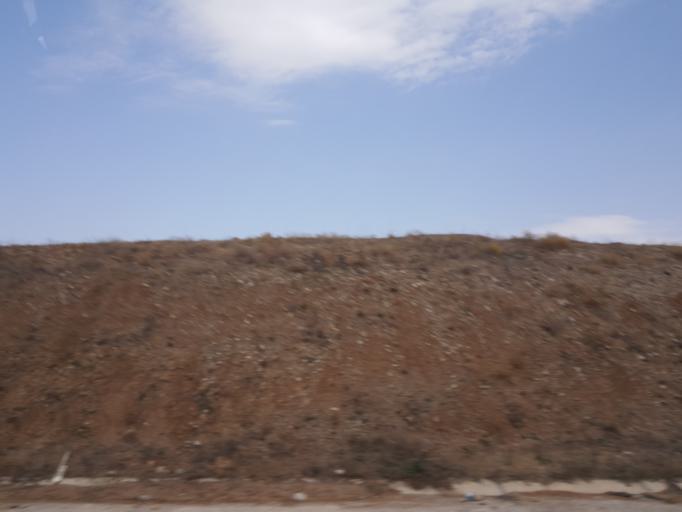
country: TR
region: Corum
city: Alaca
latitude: 40.1530
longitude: 34.7616
